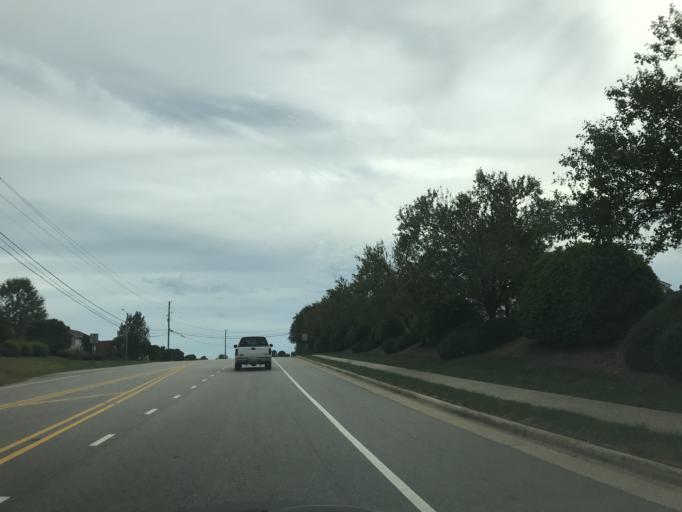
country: US
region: North Carolina
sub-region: Wake County
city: Rolesville
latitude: 35.8804
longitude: -78.5097
